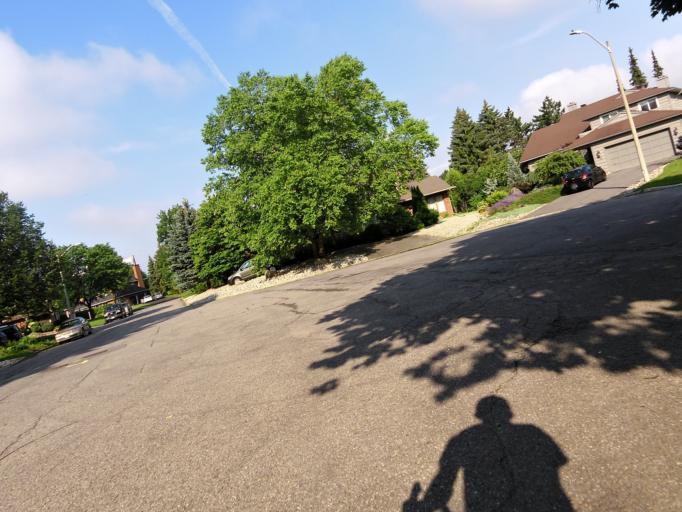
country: CA
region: Ontario
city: Ottawa
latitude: 45.3432
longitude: -75.6855
